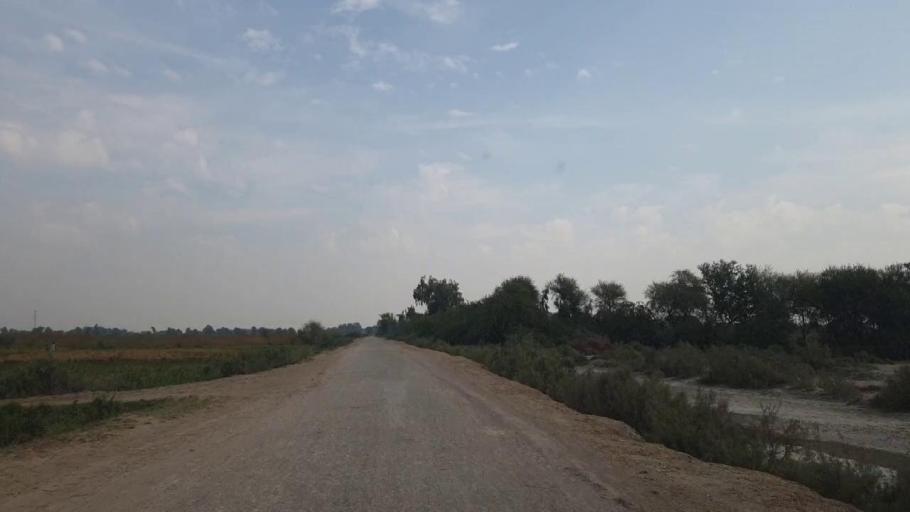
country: PK
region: Sindh
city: Rajo Khanani
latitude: 24.9585
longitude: 68.9996
